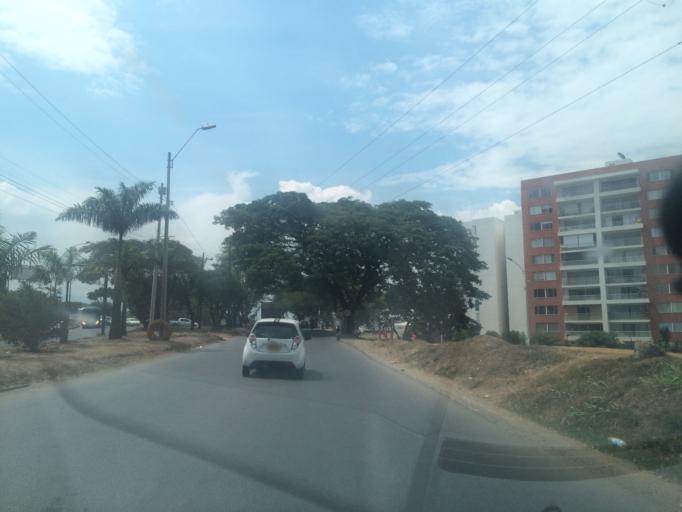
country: CO
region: Valle del Cauca
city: Cali
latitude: 3.3627
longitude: -76.5243
